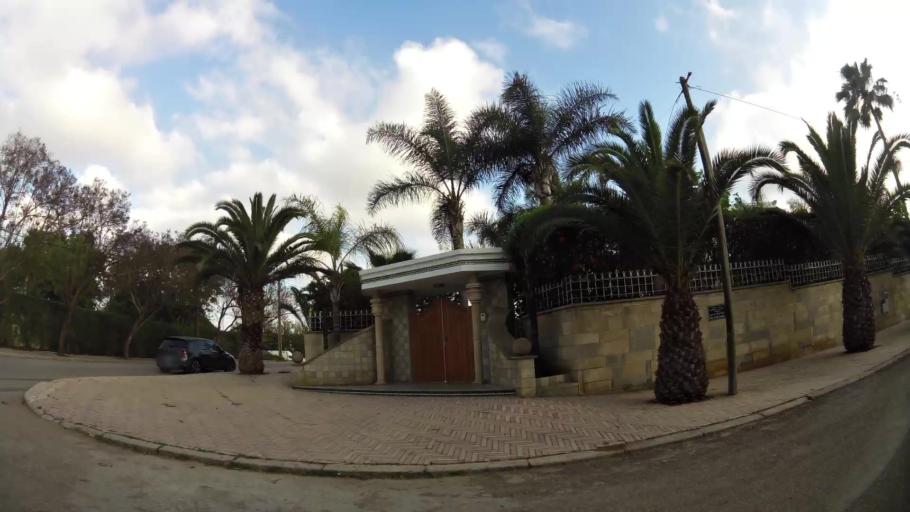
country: MA
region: Rabat-Sale-Zemmour-Zaer
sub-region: Rabat
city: Rabat
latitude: 33.9575
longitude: -6.8352
